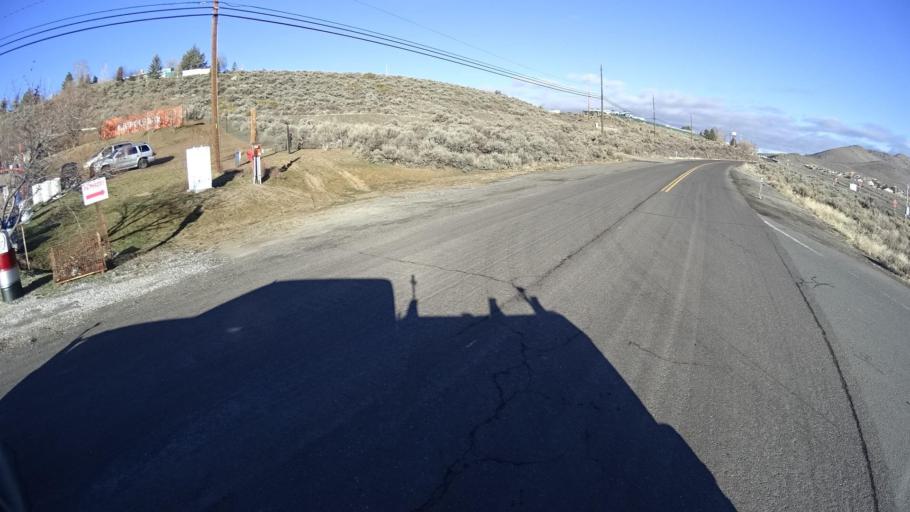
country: US
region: Nevada
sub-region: Washoe County
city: Cold Springs
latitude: 39.6674
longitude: -119.9973
